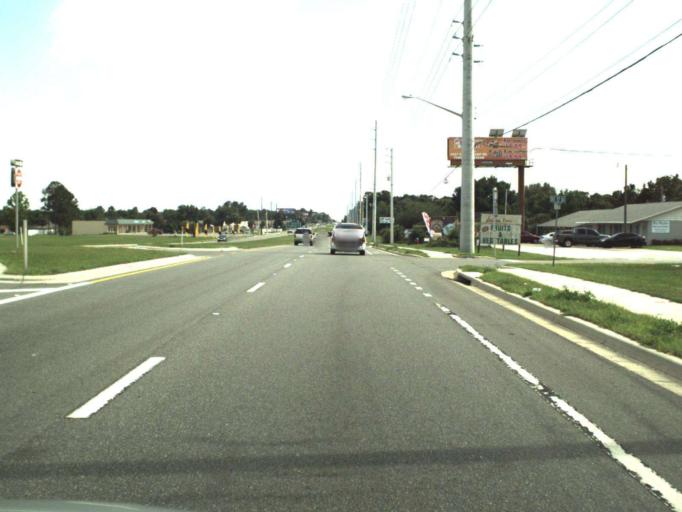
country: US
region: Florida
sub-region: Marion County
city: Silver Springs Shores
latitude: 29.1735
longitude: -82.0538
